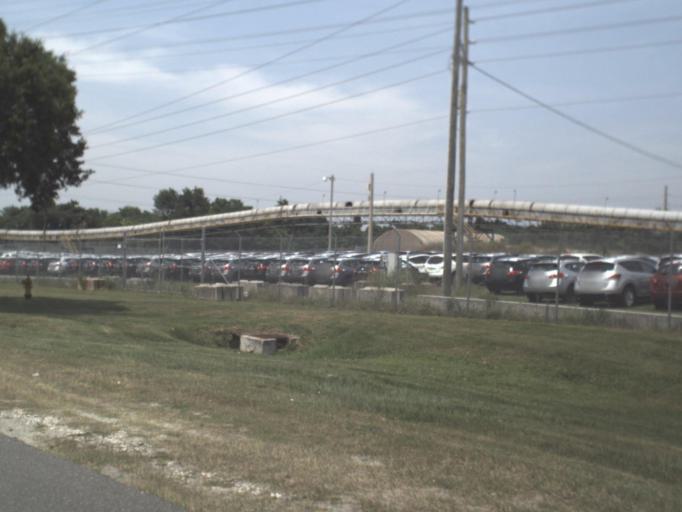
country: US
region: Florida
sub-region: Duval County
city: Jacksonville
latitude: 30.4064
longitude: -81.5366
